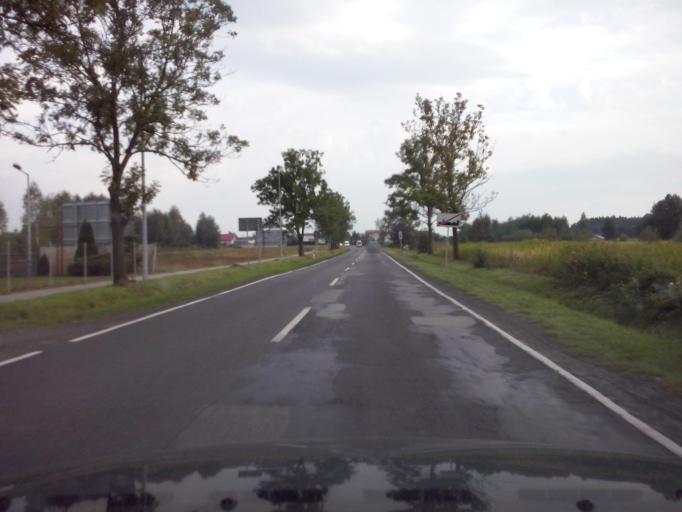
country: PL
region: Lublin Voivodeship
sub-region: Powiat bilgorajski
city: Bilgoraj
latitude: 50.5140
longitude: 22.7166
